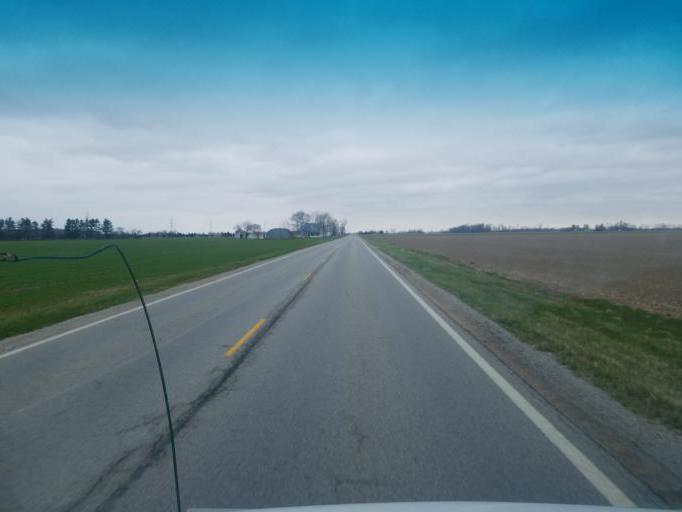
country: US
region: Ohio
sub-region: Allen County
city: Delphos
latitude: 40.9321
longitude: -84.4224
